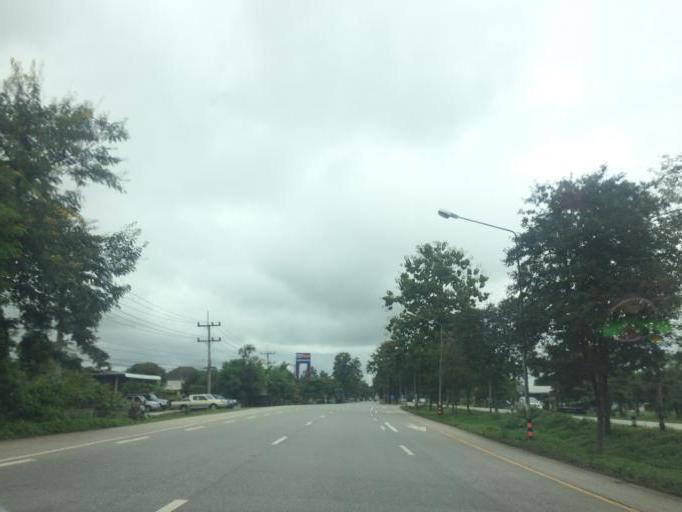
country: TH
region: Chiang Rai
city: Mae Lao
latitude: 19.8162
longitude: 99.7596
